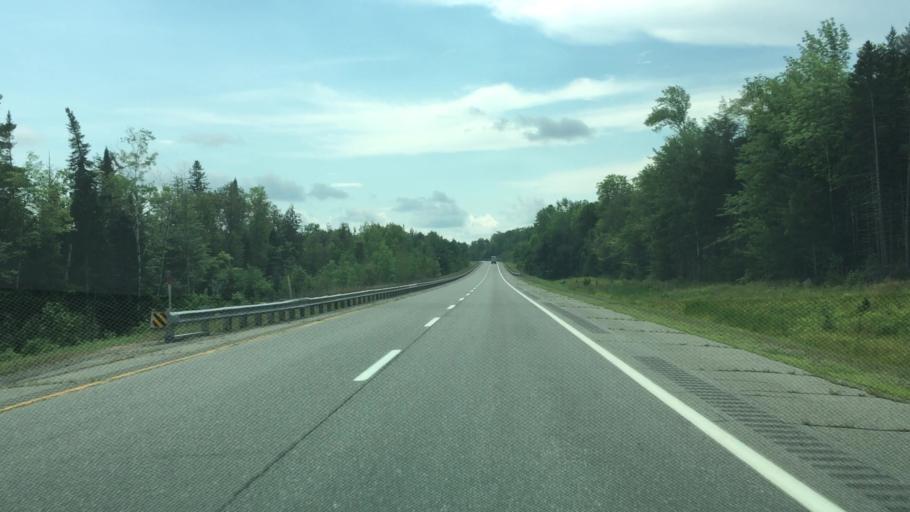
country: US
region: Maine
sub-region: Penobscot County
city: Lincoln
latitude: 45.4653
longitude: -68.5853
